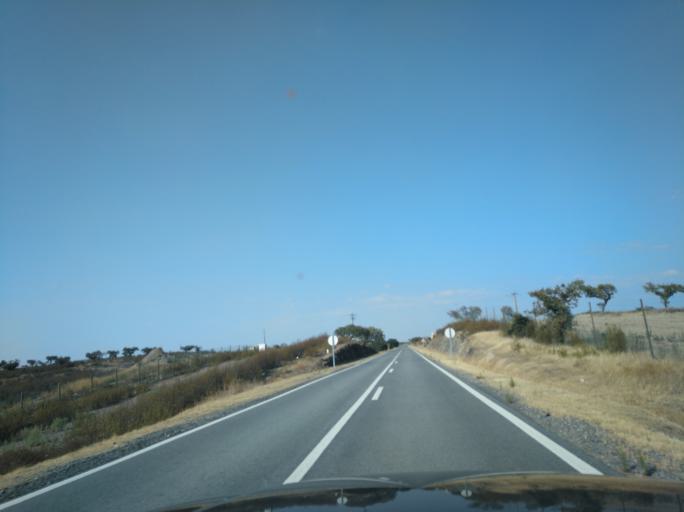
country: ES
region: Extremadura
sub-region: Provincia de Badajoz
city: Valencia del Mombuey
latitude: 38.1593
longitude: -7.2313
